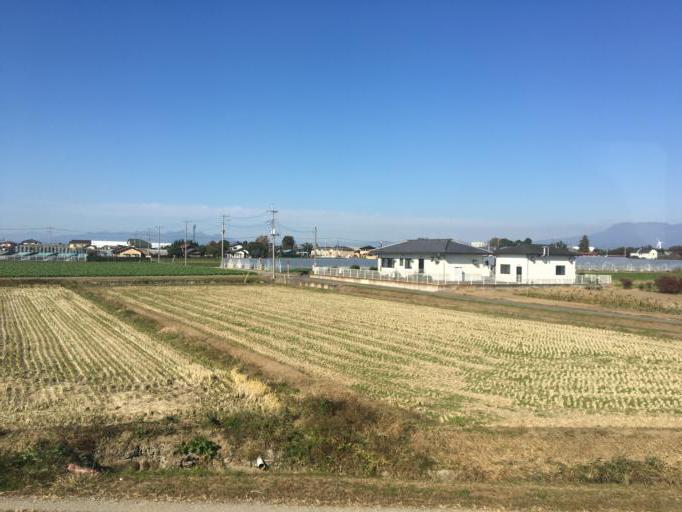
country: JP
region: Gunma
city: Isesaki
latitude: 36.3482
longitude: 139.2296
